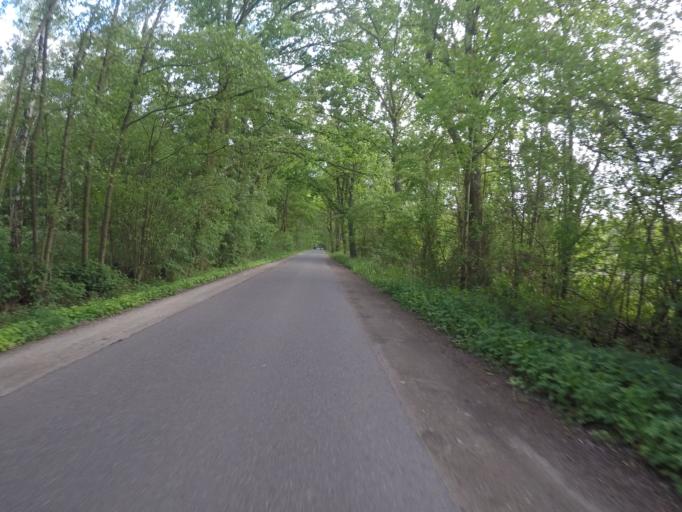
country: DE
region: Schleswig-Holstein
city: Bonningstedt
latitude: 53.6563
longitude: 9.9264
